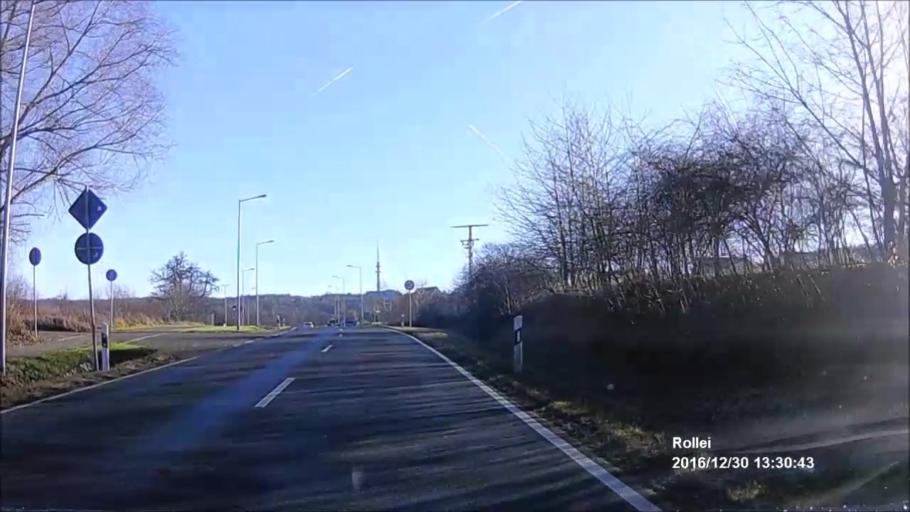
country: DE
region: Thuringia
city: Klettbach
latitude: 50.9404
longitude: 11.0990
